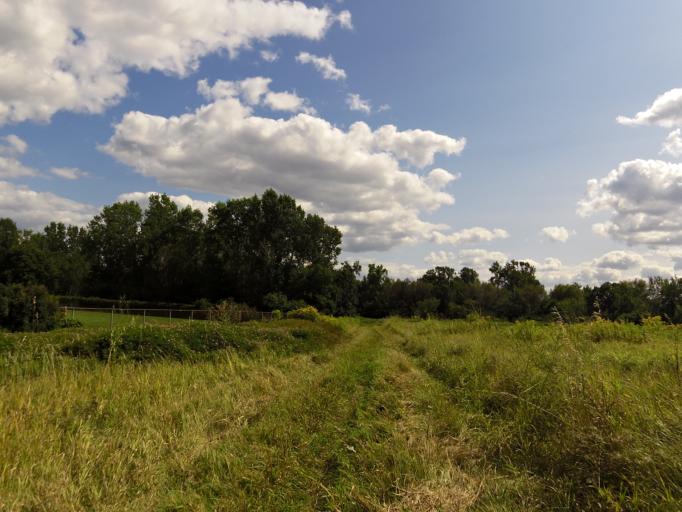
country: CA
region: Ontario
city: Bells Corners
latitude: 45.3614
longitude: -75.7809
